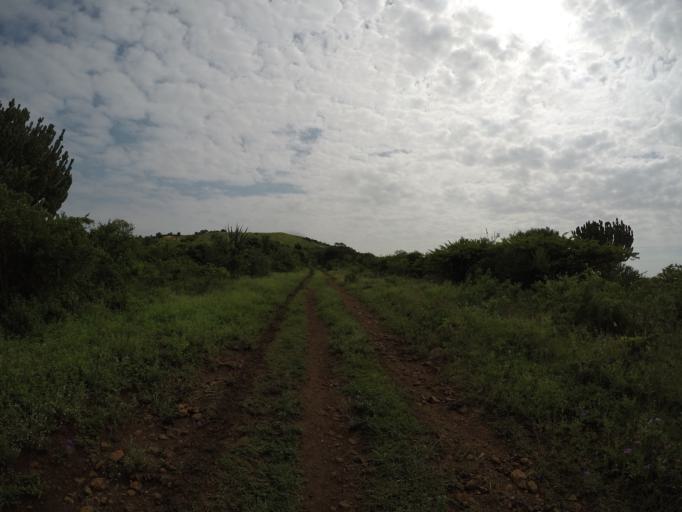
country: ZA
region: KwaZulu-Natal
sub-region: uThungulu District Municipality
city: Empangeni
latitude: -28.6235
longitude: 31.8943
